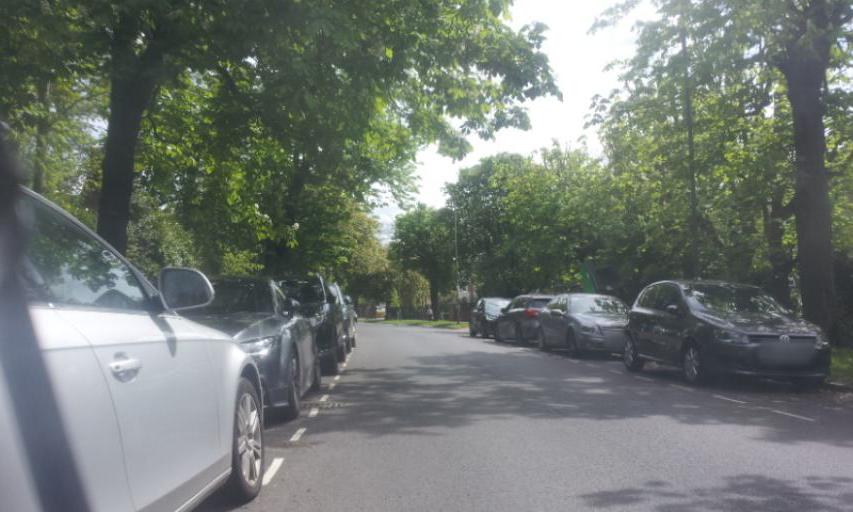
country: GB
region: England
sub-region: Greater London
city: Beckenham
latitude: 51.4134
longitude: -0.0262
